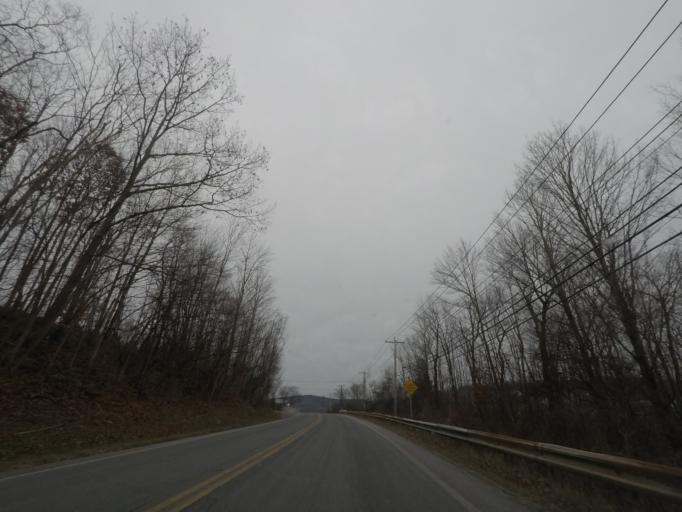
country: US
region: Massachusetts
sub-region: Berkshire County
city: Williamstown
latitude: 42.6781
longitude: -73.2347
